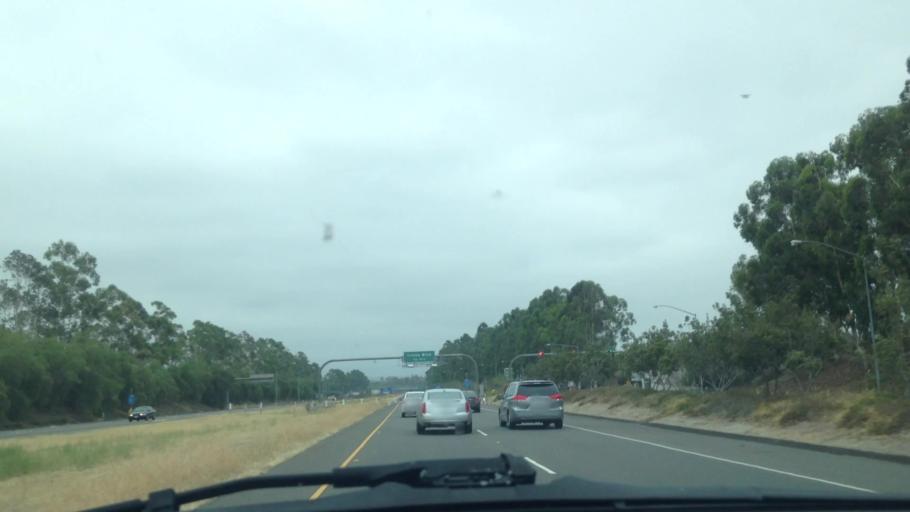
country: US
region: California
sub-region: Orange County
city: North Tustin
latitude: 33.7376
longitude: -117.7698
